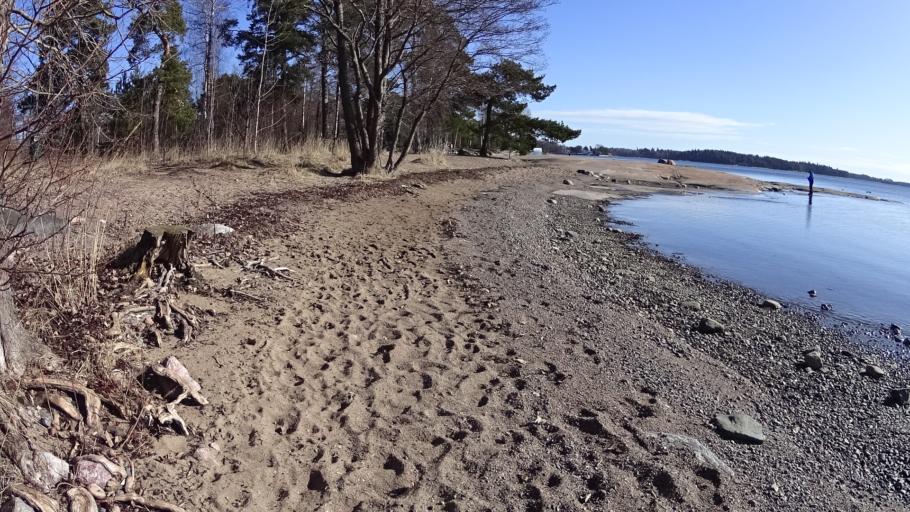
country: FI
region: Uusimaa
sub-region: Helsinki
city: Koukkuniemi
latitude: 60.1532
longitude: 24.7716
